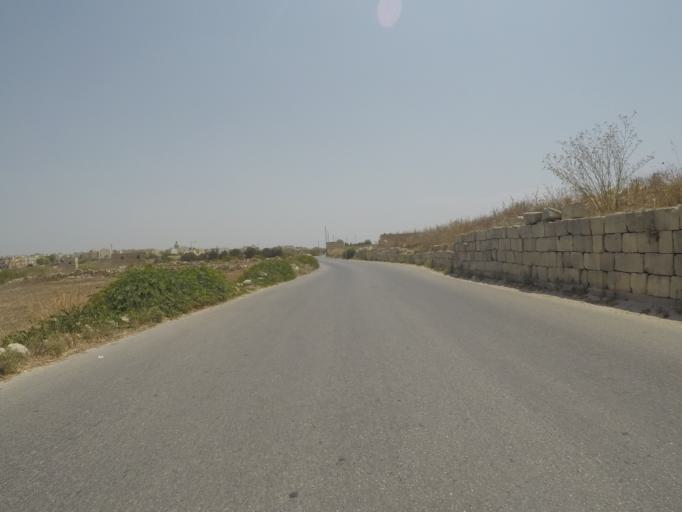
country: MT
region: Is-Siggiewi
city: Siggiewi
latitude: 35.8554
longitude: 14.4260
